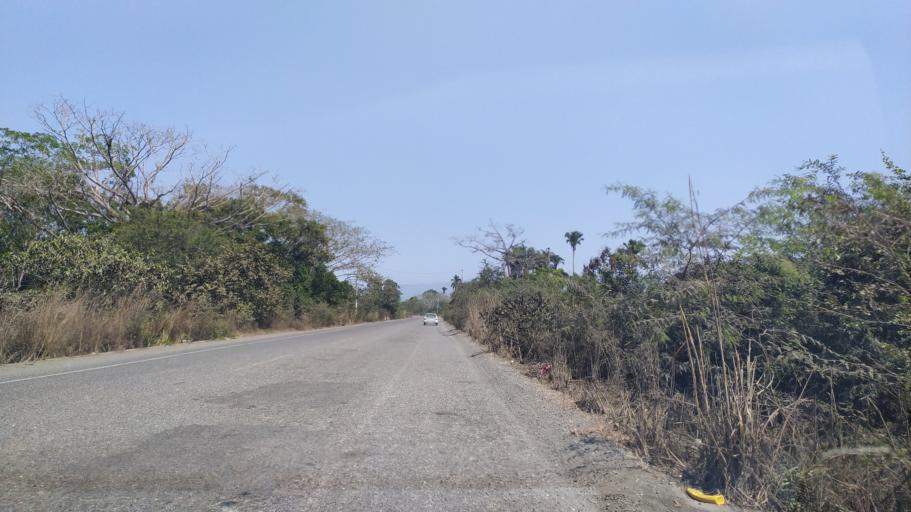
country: MX
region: Michoacan
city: Coahuayana Viejo
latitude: 18.6518
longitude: -103.6716
